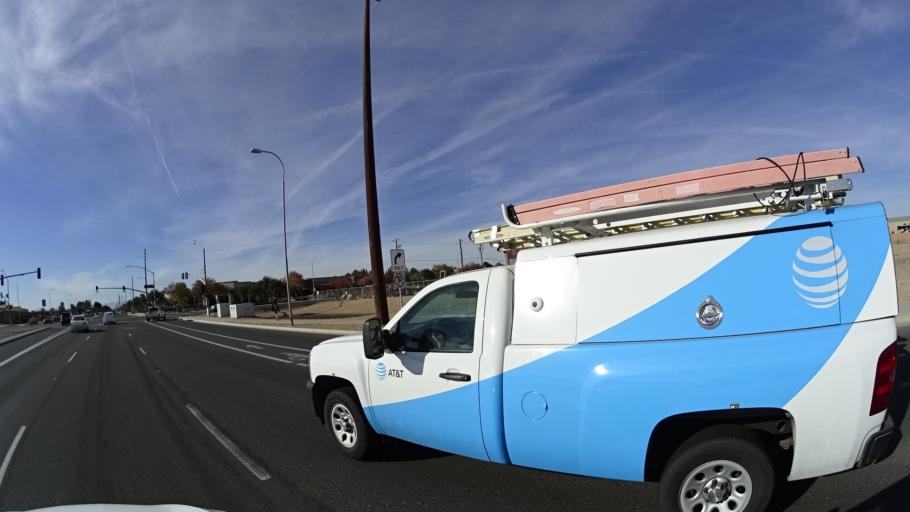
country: US
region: Arizona
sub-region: Maricopa County
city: Sun Lakes
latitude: 33.2193
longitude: -111.7720
